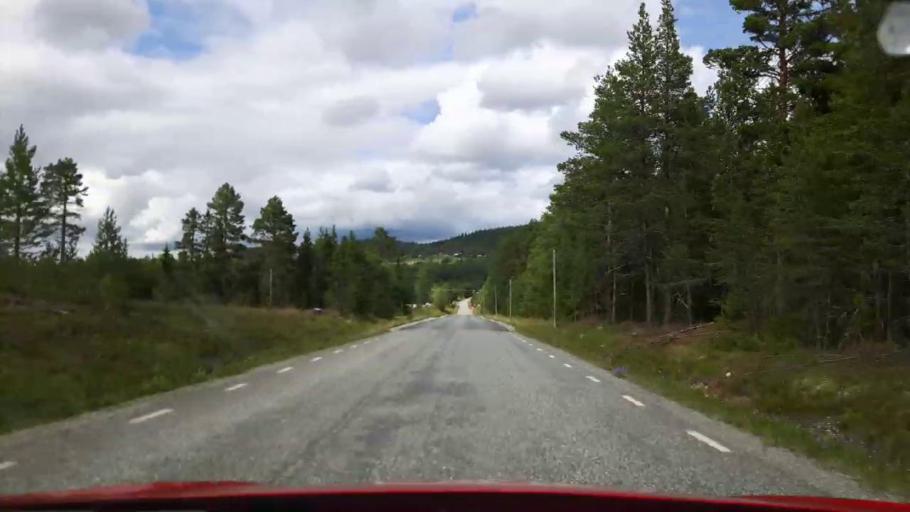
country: NO
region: Hedmark
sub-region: Engerdal
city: Engerdal
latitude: 62.4305
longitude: 12.6802
